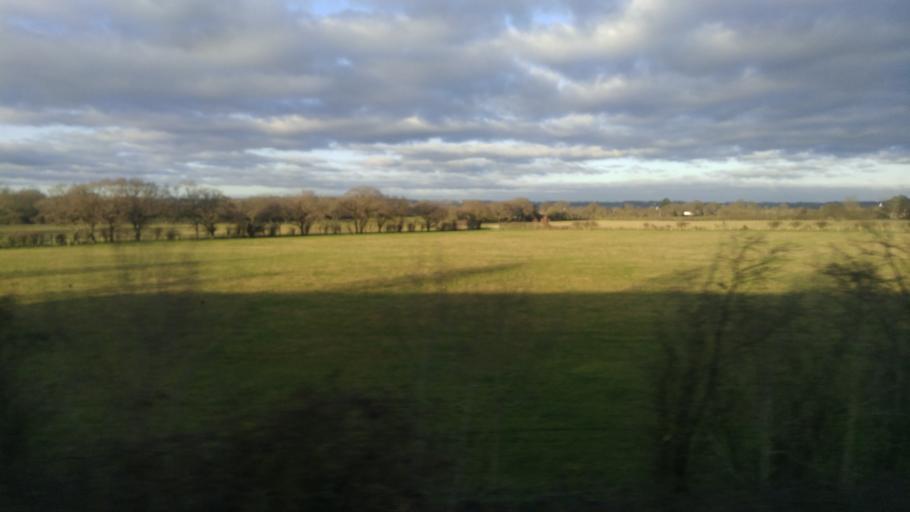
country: GB
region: England
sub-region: Kent
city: Headcorn
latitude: 51.1624
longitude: 0.6704
